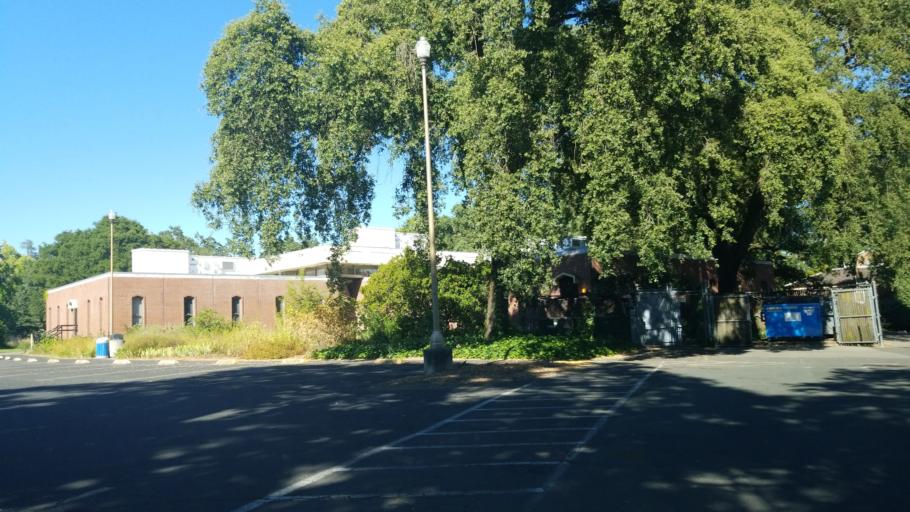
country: US
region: California
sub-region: Sonoma County
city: Santa Rosa
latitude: 38.4551
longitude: -122.7215
